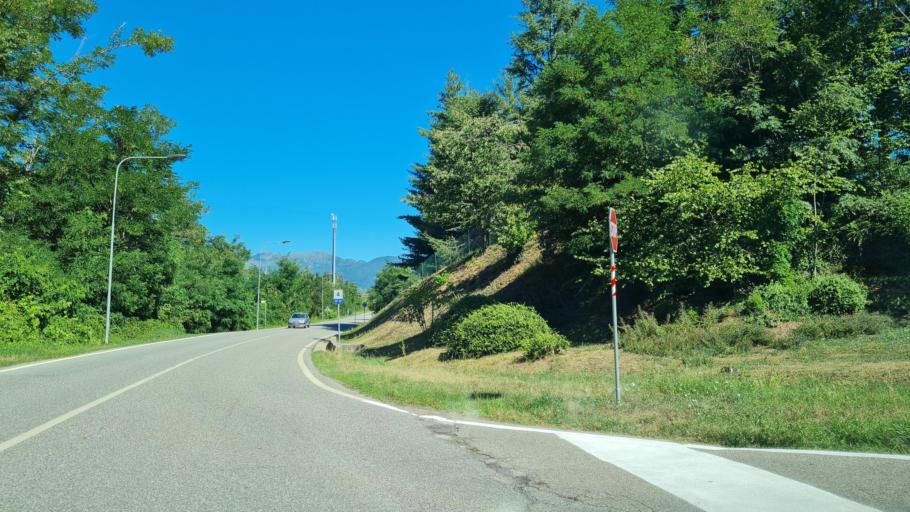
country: IT
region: Piedmont
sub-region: Provincia di Biella
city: Lessona
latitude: 45.5860
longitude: 8.1993
